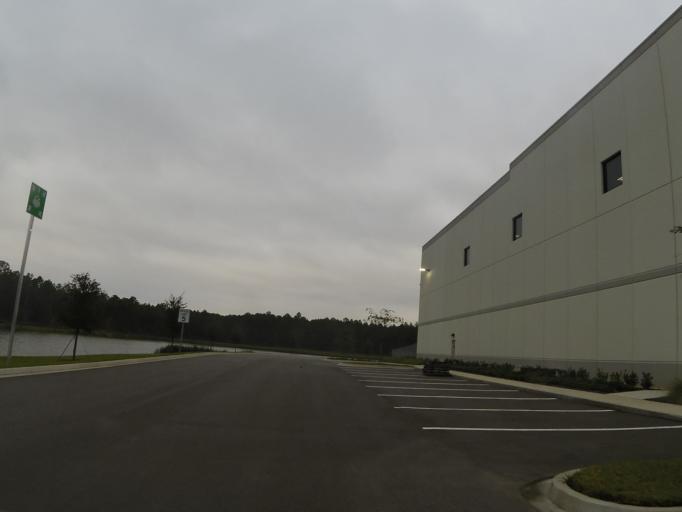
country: US
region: Florida
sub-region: Duval County
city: Baldwin
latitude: 30.2486
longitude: -81.8669
